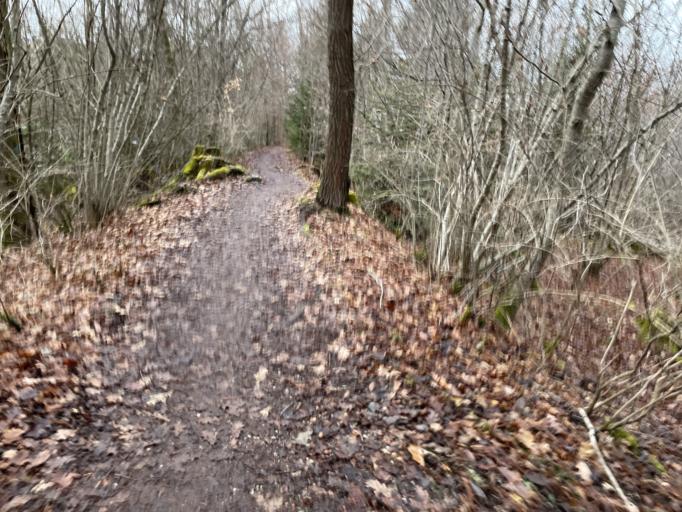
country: CH
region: Bern
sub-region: Thun District
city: Uttigen
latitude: 46.8000
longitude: 7.5715
